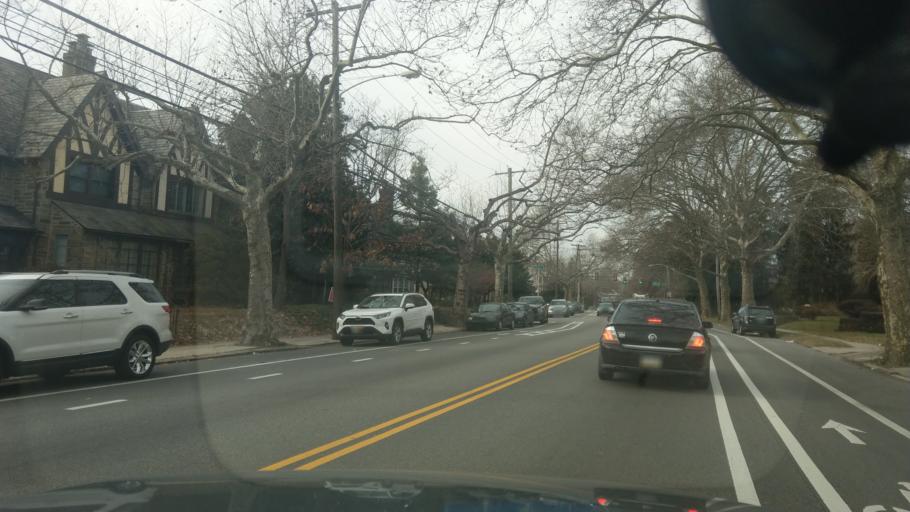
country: US
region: Pennsylvania
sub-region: Montgomery County
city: Jenkintown
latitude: 40.0459
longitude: -75.1306
